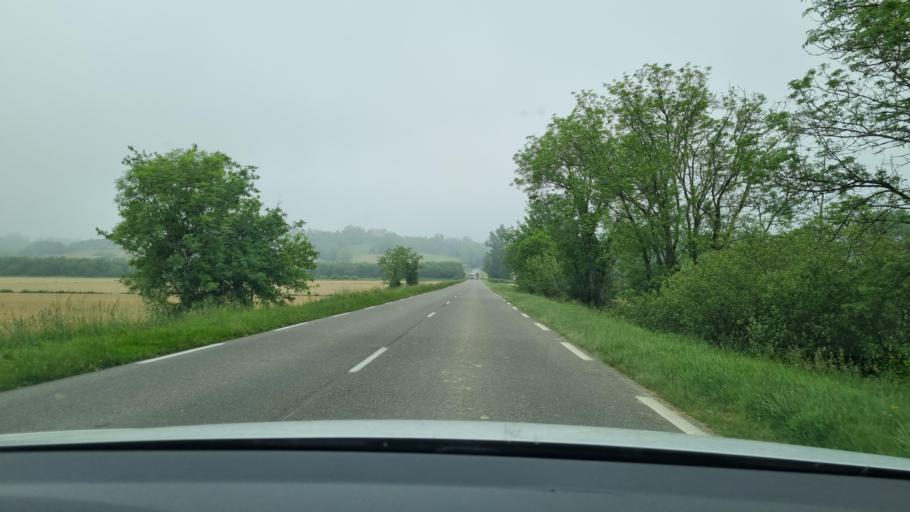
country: FR
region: Aquitaine
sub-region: Departement des Landes
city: Hagetmau
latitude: 43.6027
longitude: -0.6424
